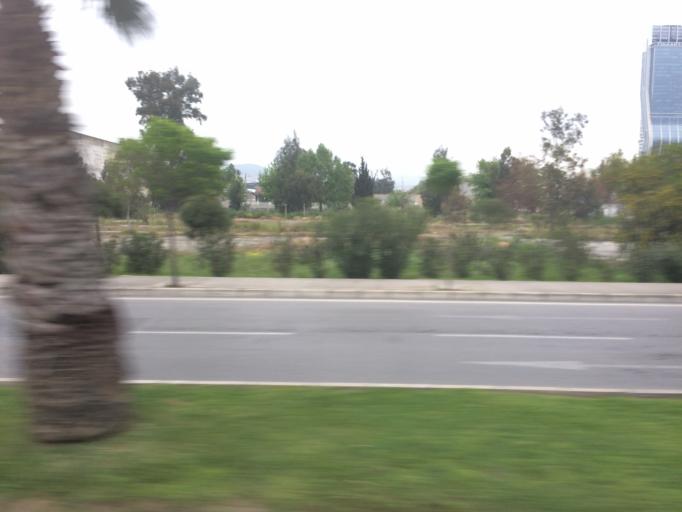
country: TR
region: Izmir
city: Izmir
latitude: 38.4547
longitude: 27.1681
